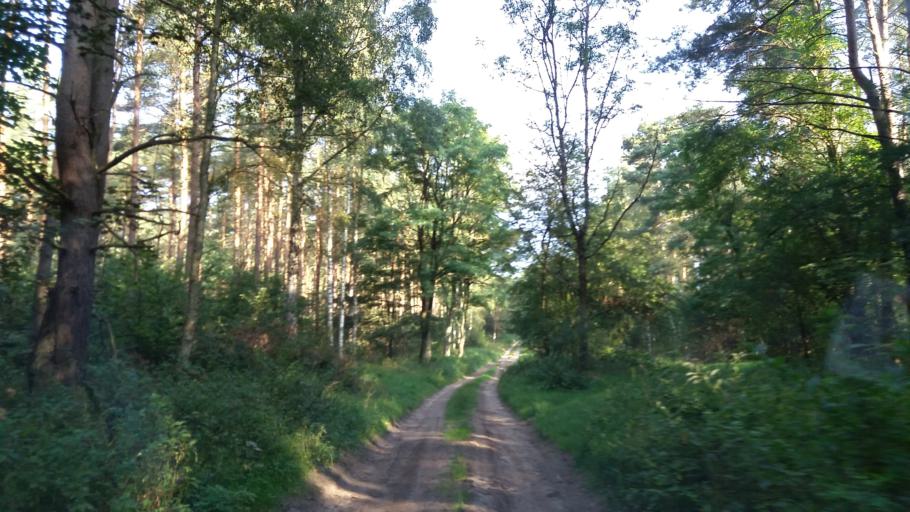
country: PL
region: West Pomeranian Voivodeship
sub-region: Powiat choszczenski
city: Recz
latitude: 53.1998
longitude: 15.5421
